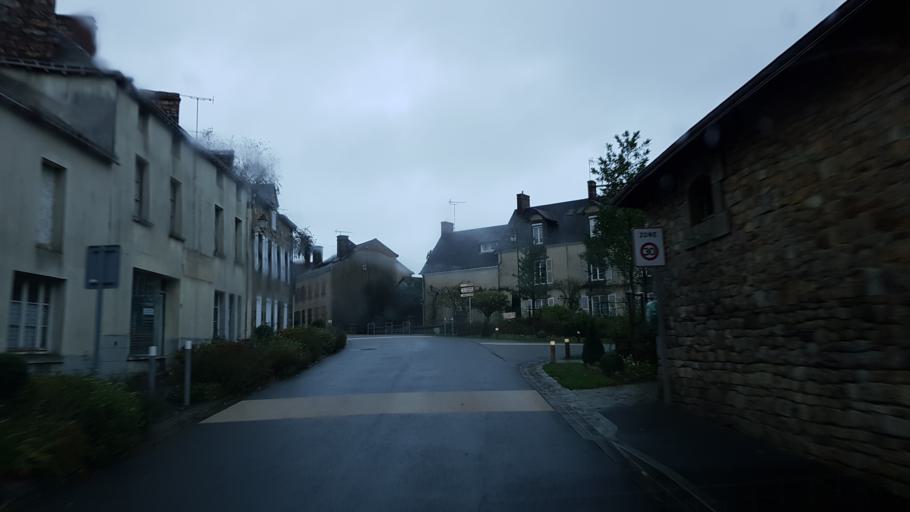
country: FR
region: Pays de la Loire
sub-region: Departement de la Mayenne
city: Juvigne
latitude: 48.2290
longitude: -1.0361
